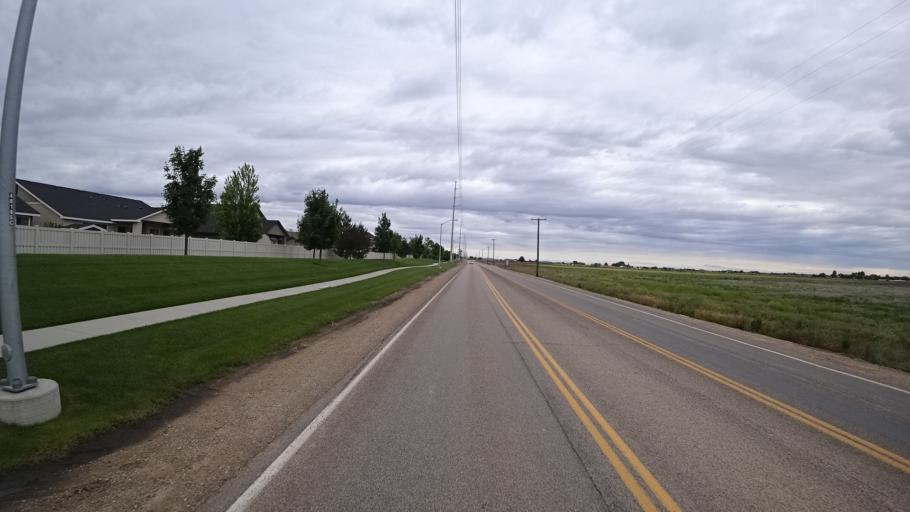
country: US
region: Idaho
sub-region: Ada County
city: Star
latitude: 43.6485
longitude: -116.4569
